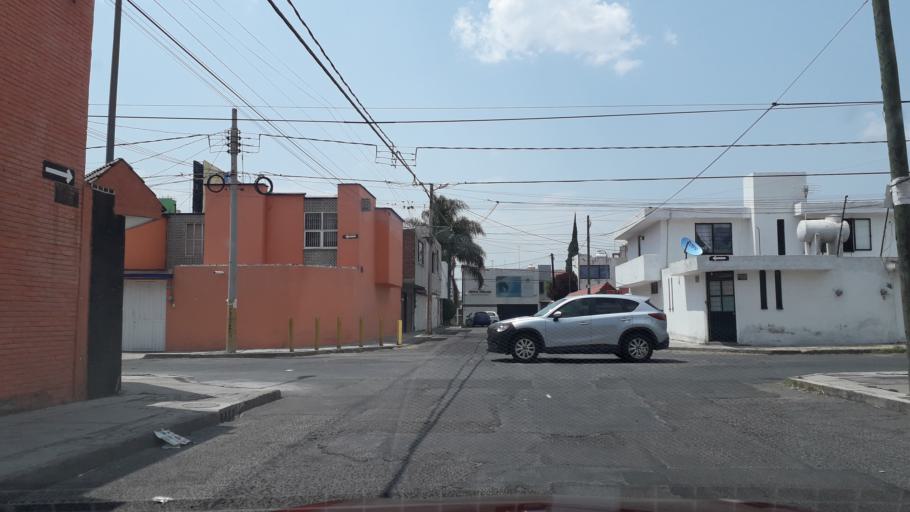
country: MX
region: Puebla
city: Puebla
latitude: 19.0348
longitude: -98.2204
